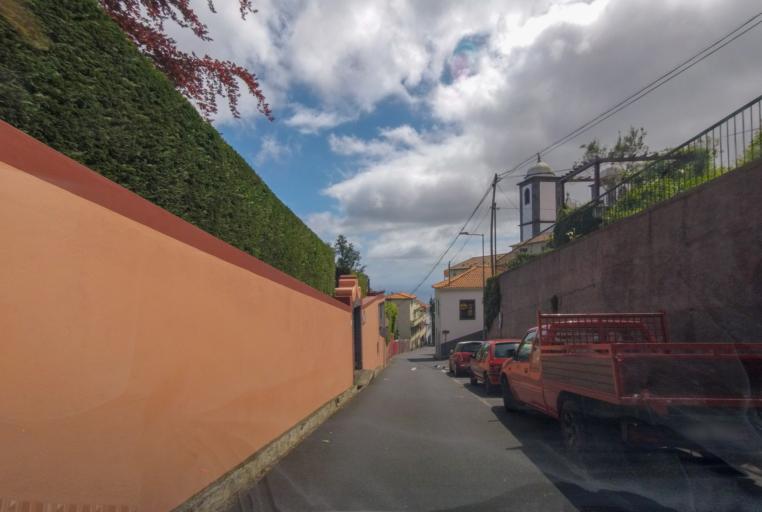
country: PT
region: Madeira
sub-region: Funchal
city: Nossa Senhora do Monte
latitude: 32.6763
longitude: -16.9020
